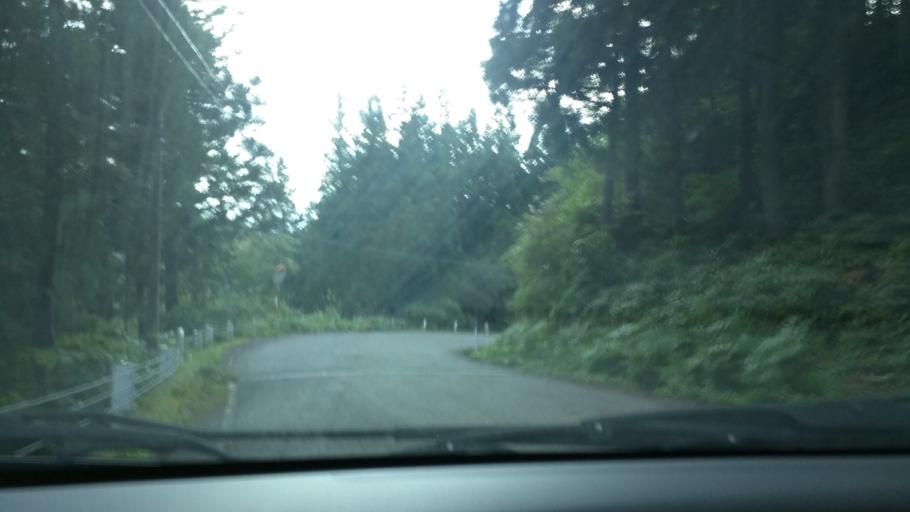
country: JP
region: Fukushima
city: Kitakata
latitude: 37.4560
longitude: 139.7196
